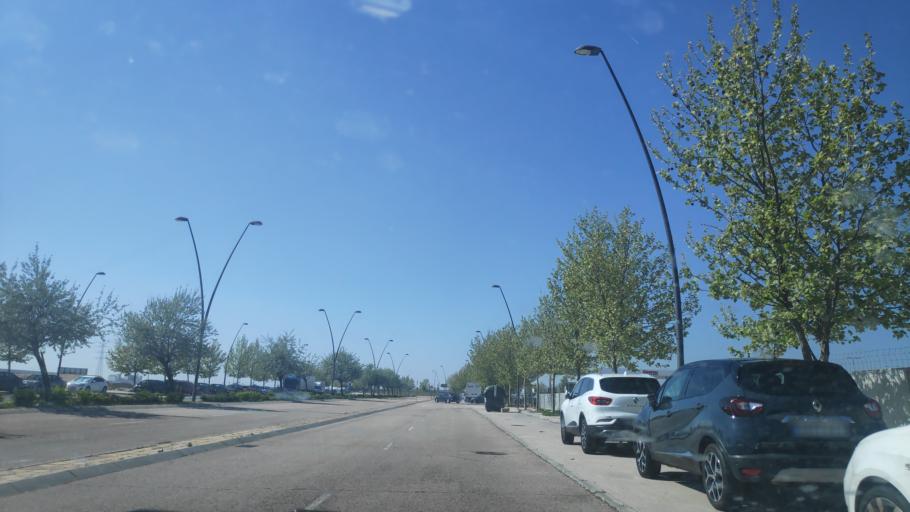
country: ES
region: Madrid
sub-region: Provincia de Madrid
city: Pinto
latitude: 40.2836
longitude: -3.6858
